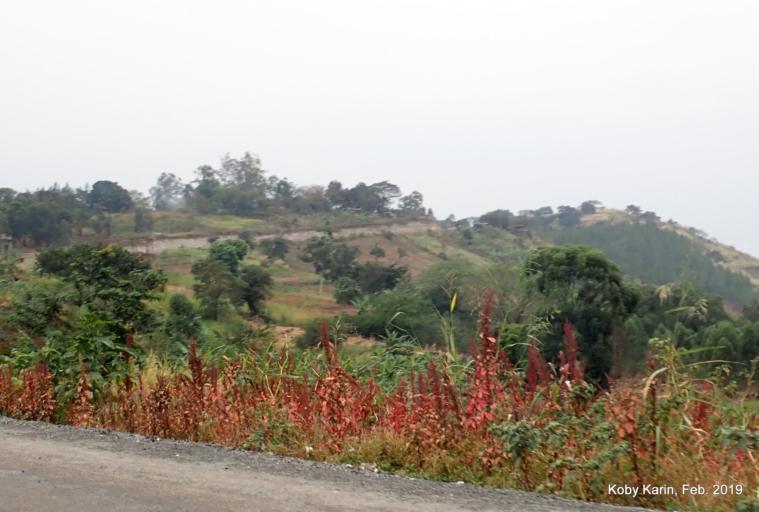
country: UG
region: Western Region
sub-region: Rubirizi District
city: Rubirizi
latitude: -0.2196
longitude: 30.0979
